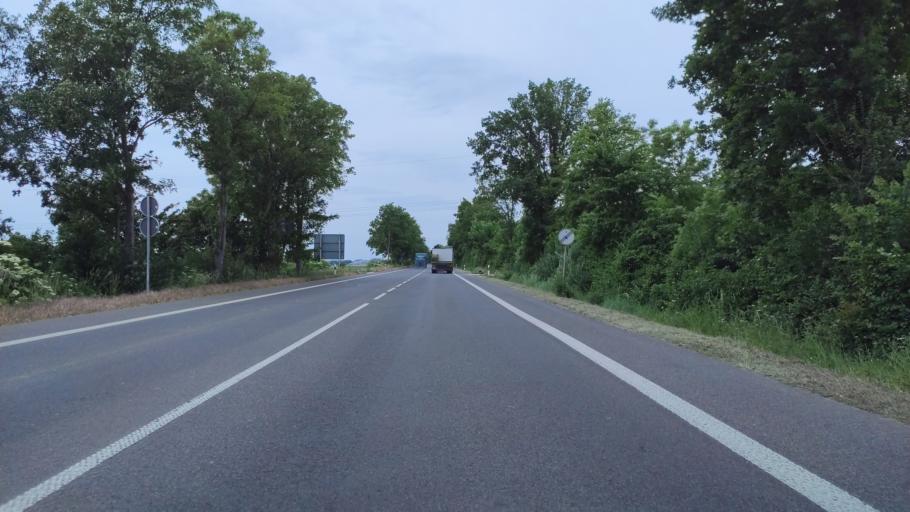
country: DE
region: North Rhine-Westphalia
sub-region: Regierungsbezirk Dusseldorf
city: Kaarst
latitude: 51.1771
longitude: 6.5872
